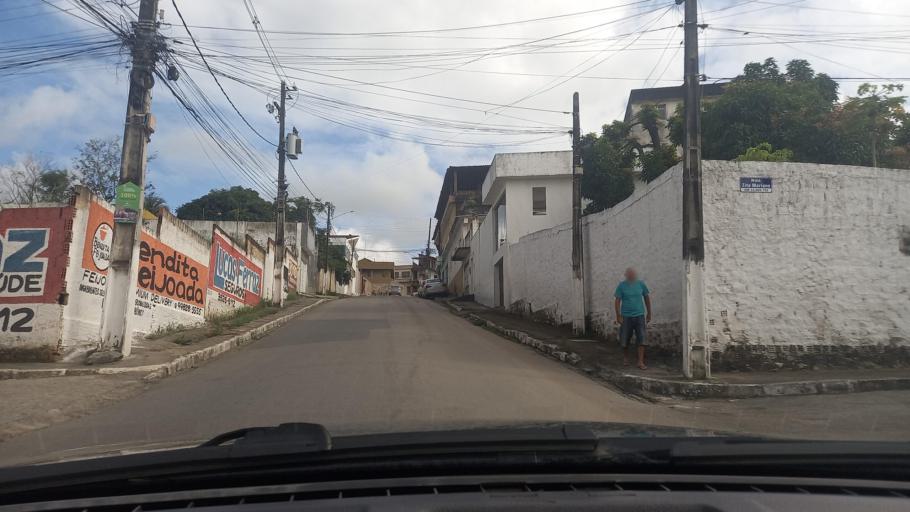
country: BR
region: Pernambuco
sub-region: Vitoria De Santo Antao
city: Vitoria de Santo Antao
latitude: -8.1128
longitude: -35.2953
